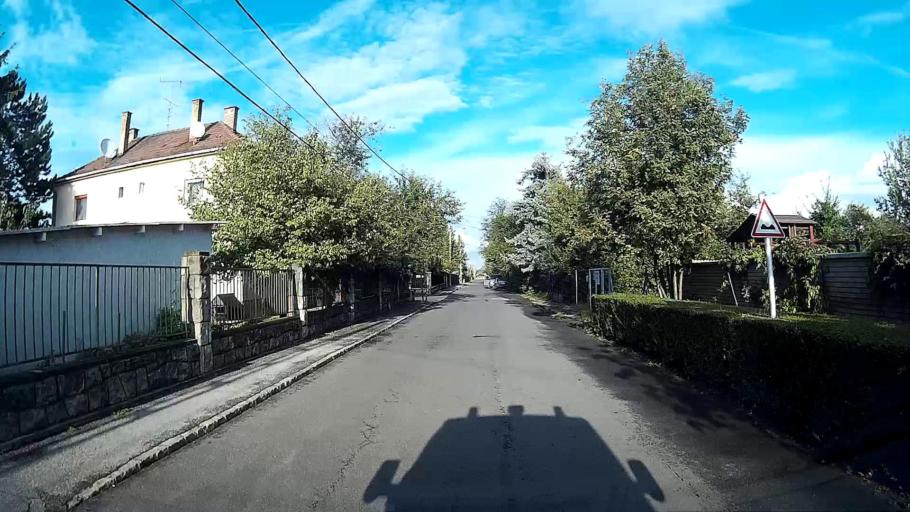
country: HU
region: Pest
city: Budakalasz
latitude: 47.6253
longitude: 19.0485
